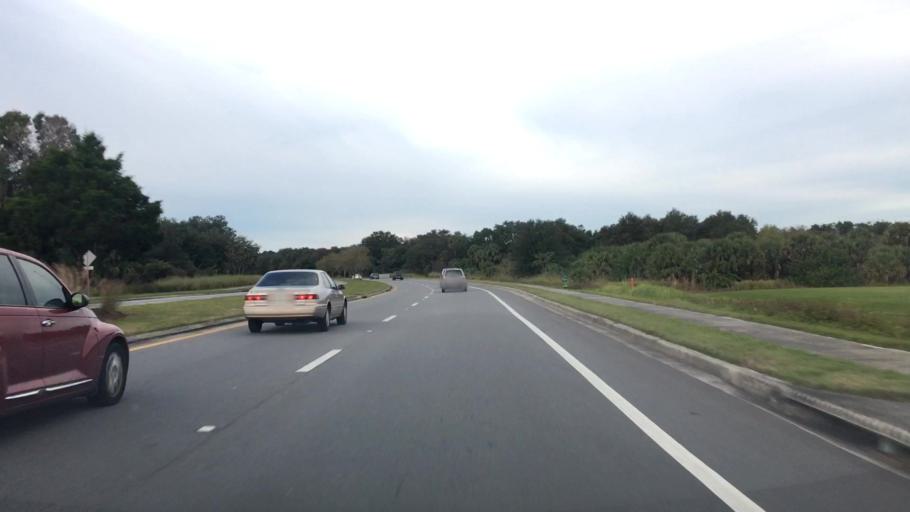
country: US
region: Florida
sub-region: Seminole County
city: Midway
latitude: 28.7606
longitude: -81.2244
